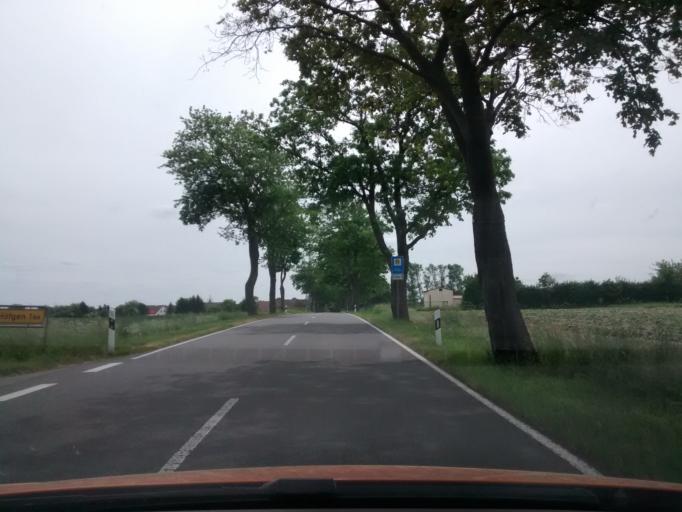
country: DE
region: Brandenburg
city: Juterbog
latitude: 51.9094
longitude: 13.1377
